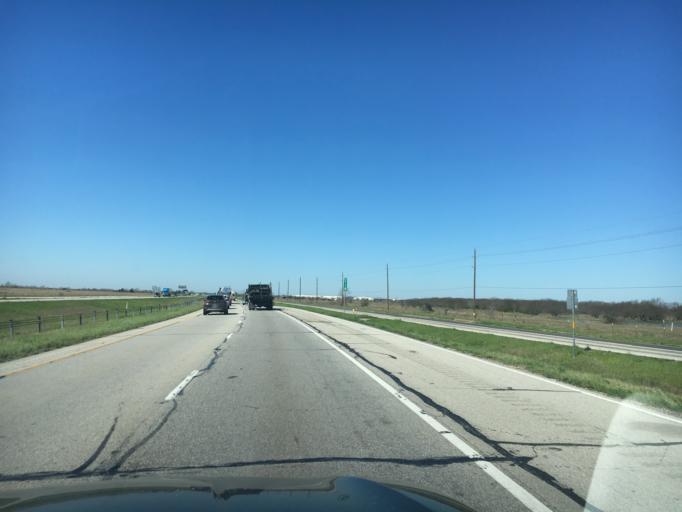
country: US
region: Texas
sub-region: Austin County
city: Sealy
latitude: 29.7639
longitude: -96.1907
